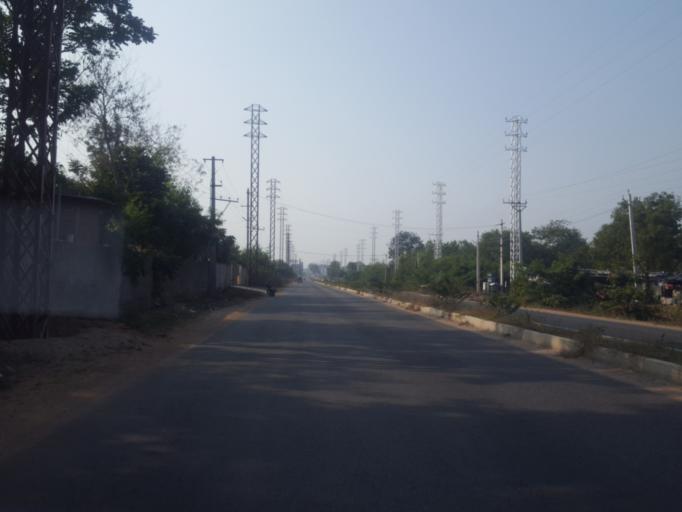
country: IN
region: Telangana
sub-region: Medak
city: Serilingampalle
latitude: 17.4013
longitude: 78.2935
